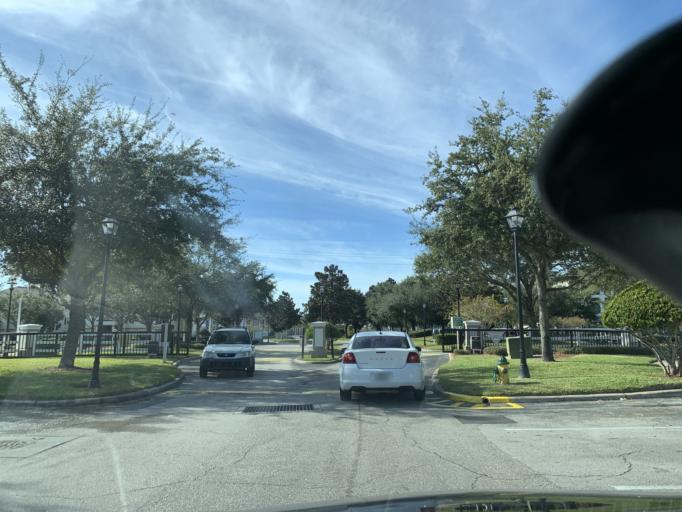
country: US
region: Florida
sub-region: Orange County
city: Oak Ridge
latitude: 28.4782
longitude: -81.4406
